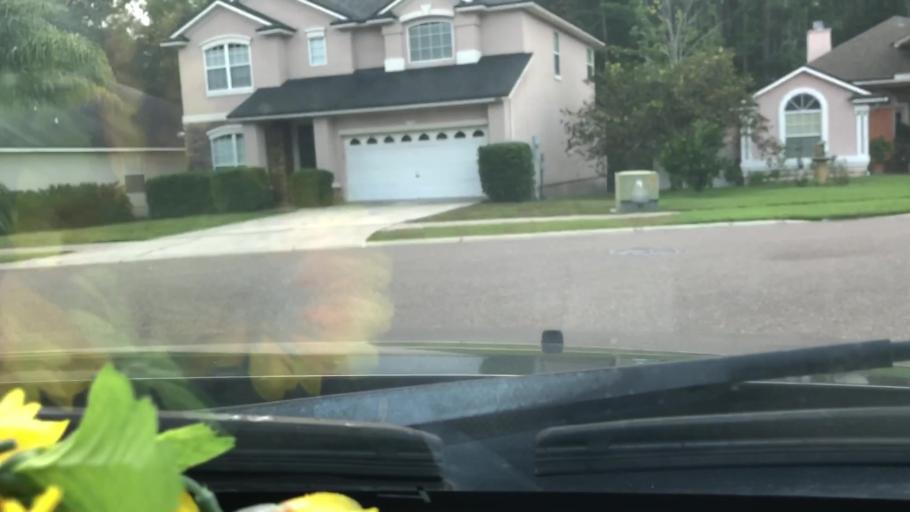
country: US
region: Florida
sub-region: Duval County
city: Atlantic Beach
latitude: 30.3369
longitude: -81.4930
